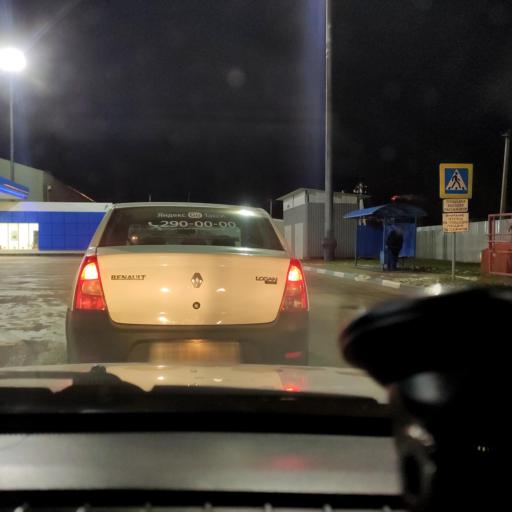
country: RU
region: Perm
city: Froly
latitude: 57.9579
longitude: 56.2874
